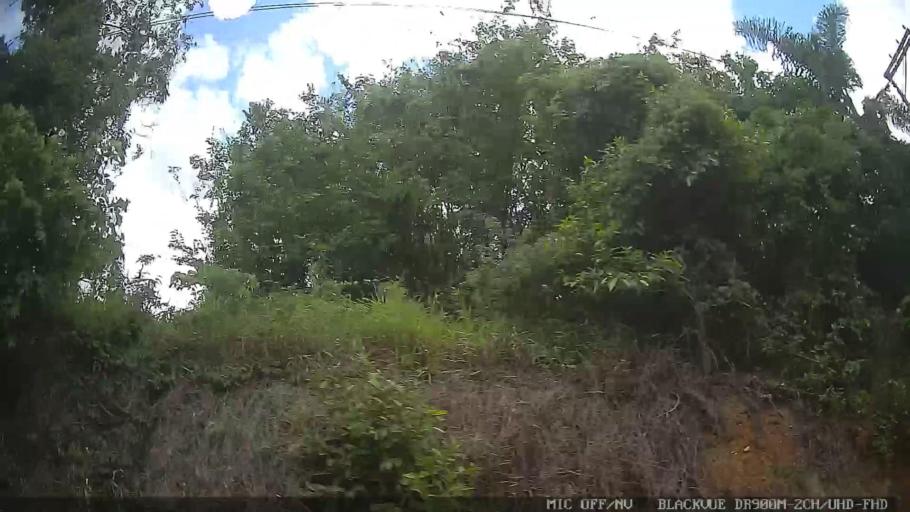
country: BR
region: Sao Paulo
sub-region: Serra Negra
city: Serra Negra
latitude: -22.6018
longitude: -46.7002
